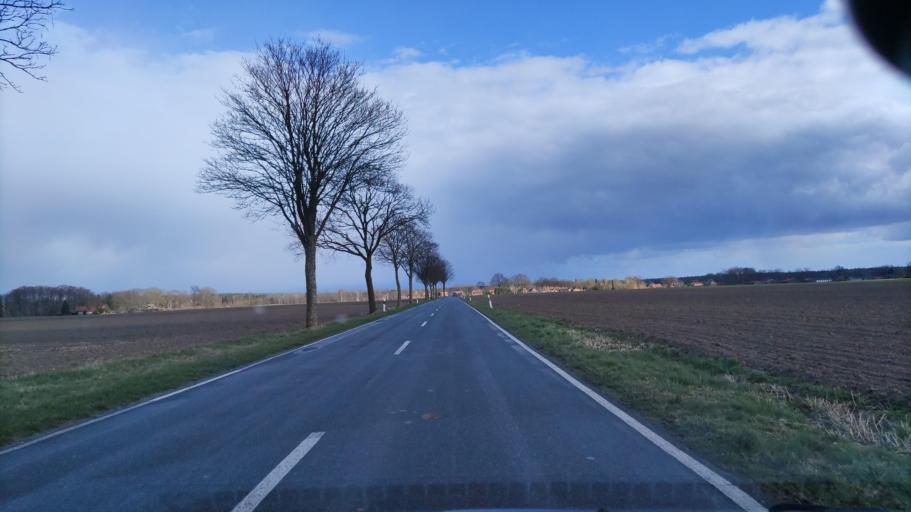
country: DE
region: Lower Saxony
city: Hermannsburg
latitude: 52.8057
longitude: 10.0728
